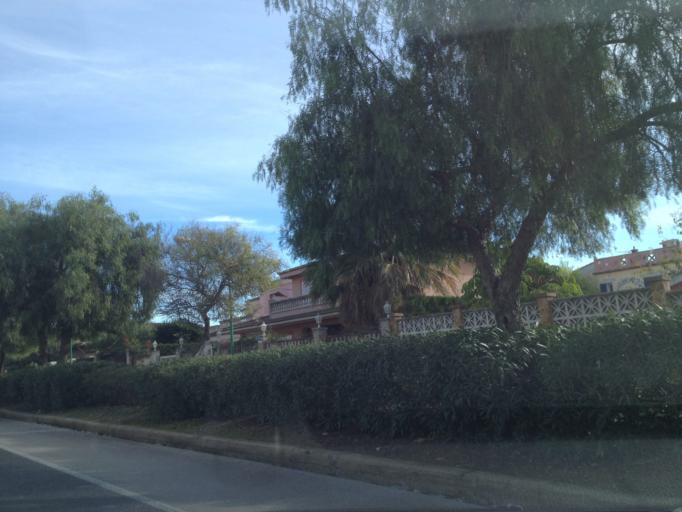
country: ES
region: Balearic Islands
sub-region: Illes Balears
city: Marratxi
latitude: 39.6207
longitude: 2.7243
